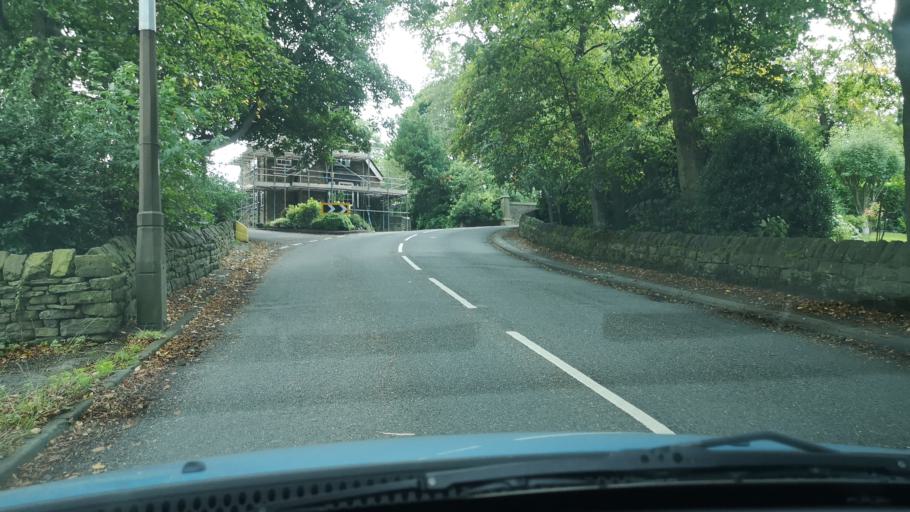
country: GB
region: England
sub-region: Kirklees
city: Mirfield
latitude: 53.6637
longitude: -1.7021
